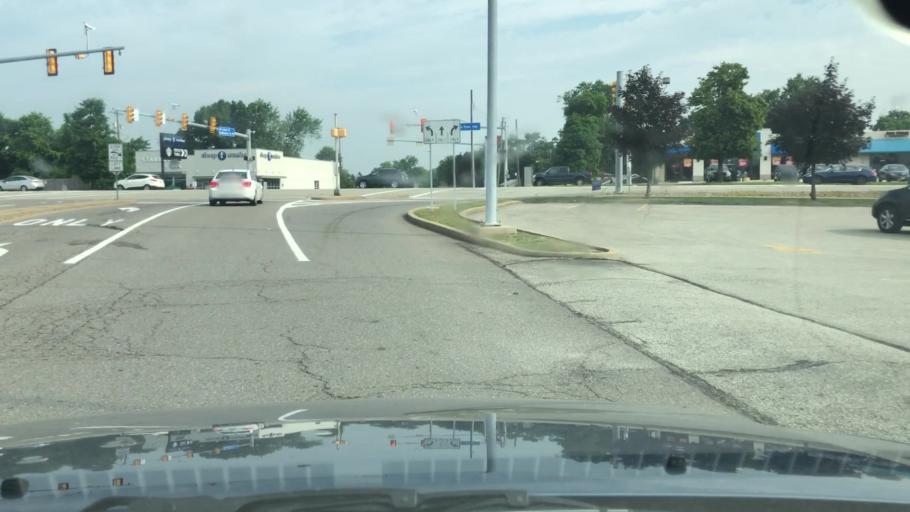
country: US
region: Pennsylvania
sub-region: Allegheny County
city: Monroeville
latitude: 40.4384
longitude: -79.7623
